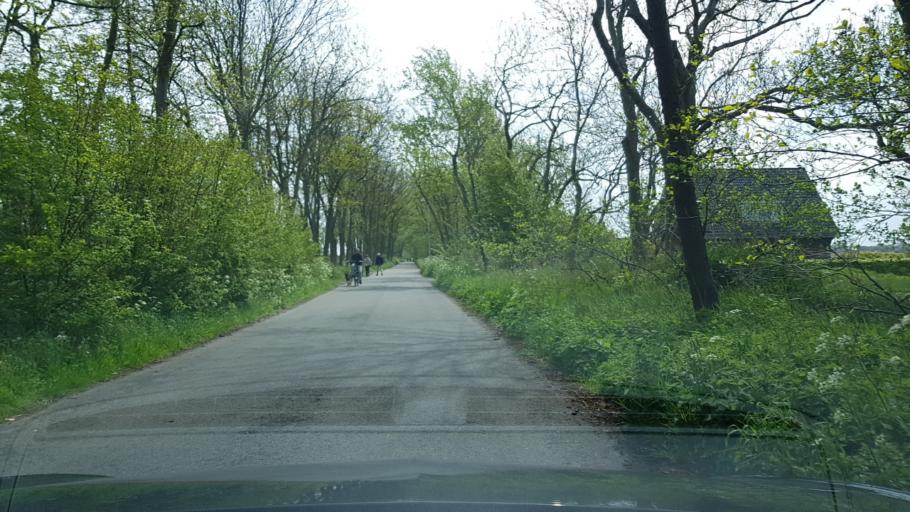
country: NL
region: South Holland
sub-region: Gemeente Teylingen
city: Sassenheim
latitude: 52.2514
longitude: 4.5265
